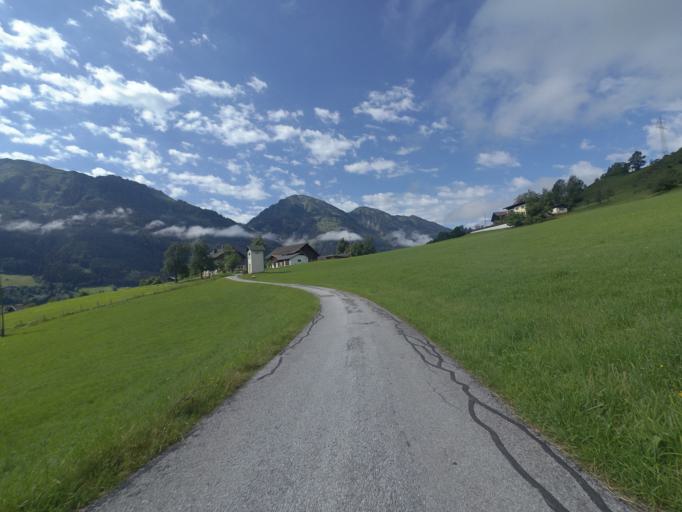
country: AT
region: Salzburg
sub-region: Politischer Bezirk Sankt Johann im Pongau
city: Schwarzach im Pongau
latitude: 47.3237
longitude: 13.1357
